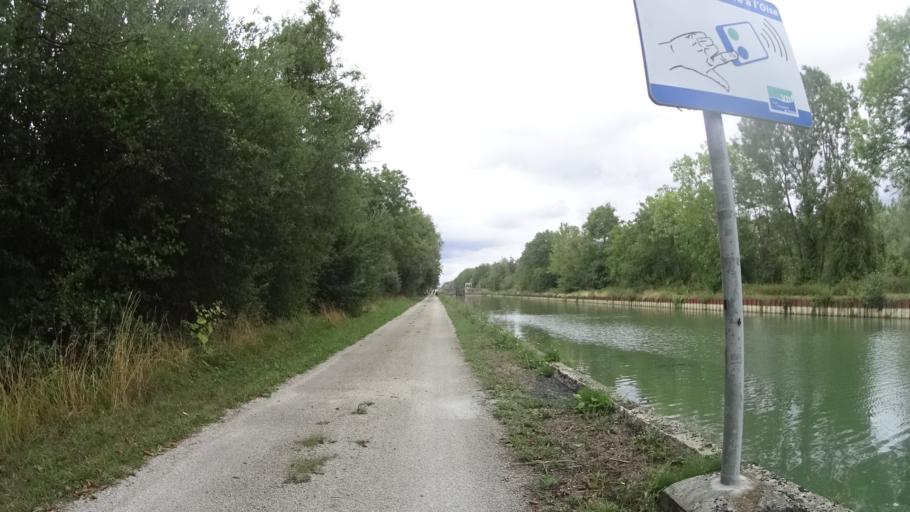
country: FR
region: Picardie
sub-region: Departement de l'Aisne
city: La Fere
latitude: 49.6976
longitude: 3.3704
